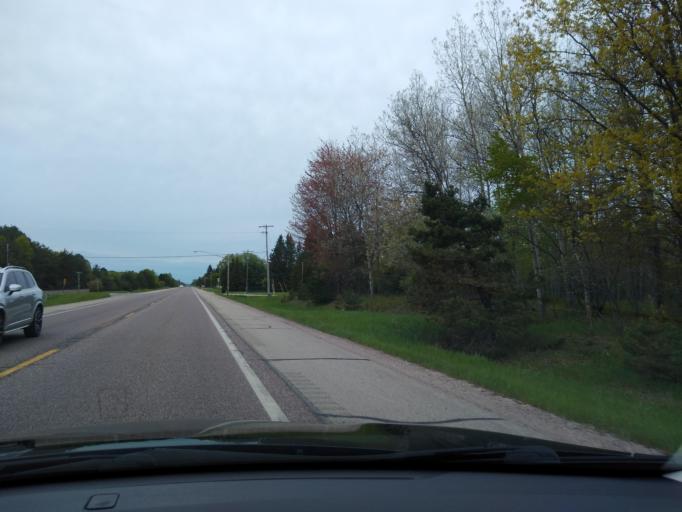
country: US
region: Michigan
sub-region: Delta County
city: Gladstone
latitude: 45.8757
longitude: -87.0641
